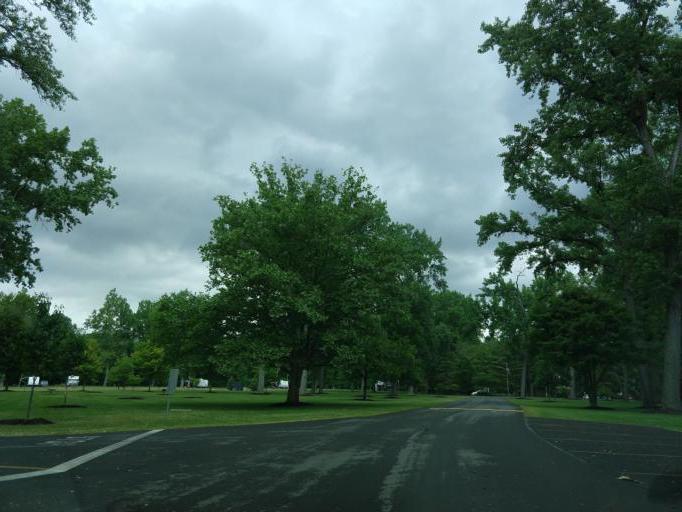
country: US
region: New York
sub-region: Tompkins County
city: Northwest Ithaca
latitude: 42.5374
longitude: -76.5467
